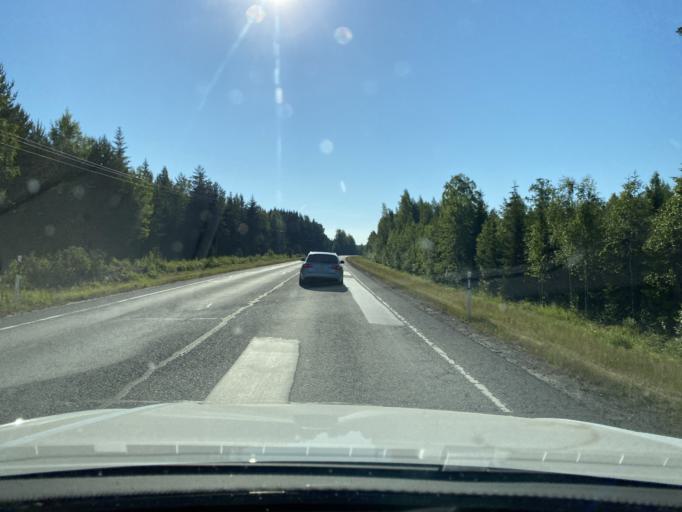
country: FI
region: Haeme
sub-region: Forssa
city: Tammela
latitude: 60.8298
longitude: 23.8735
